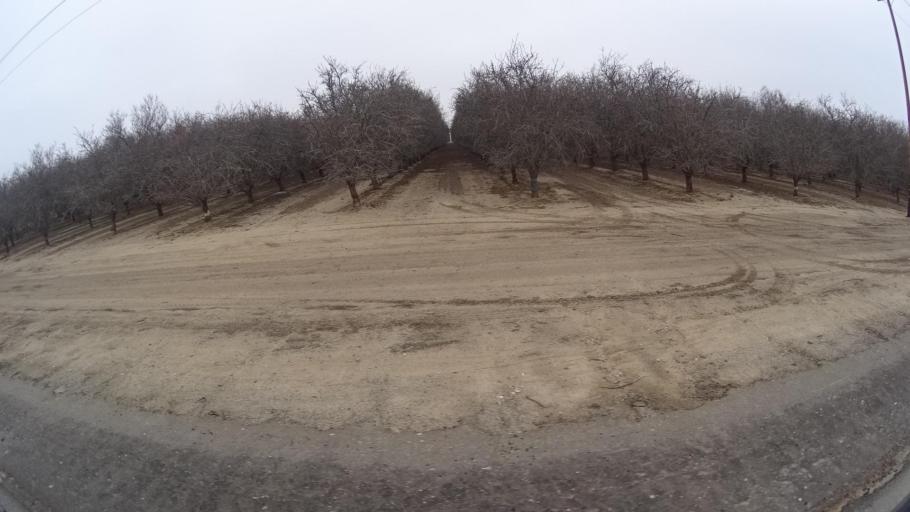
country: US
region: California
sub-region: Kern County
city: Maricopa
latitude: 35.0938
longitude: -119.2726
